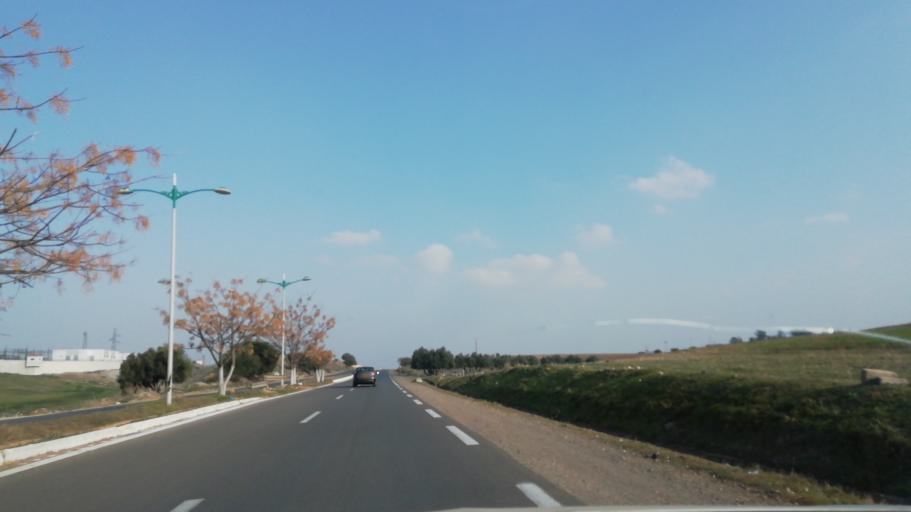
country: DZ
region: Ain Temouchent
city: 'Ain Temouchent
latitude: 35.2931
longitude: -1.1136
